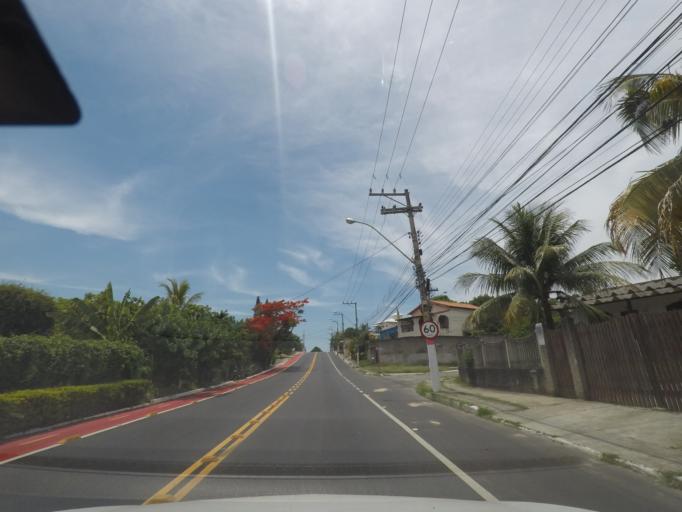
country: BR
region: Rio de Janeiro
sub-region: Marica
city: Marica
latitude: -22.9421
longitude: -42.8275
